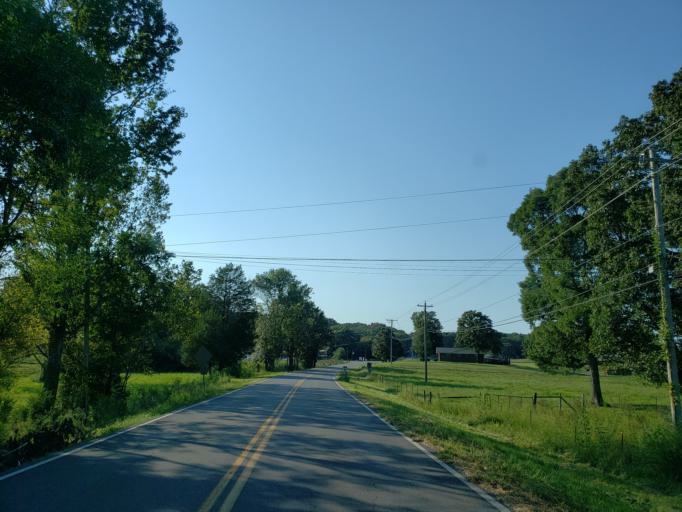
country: US
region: Tennessee
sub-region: Bradley County
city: Wildwood Lake
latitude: 35.0883
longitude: -84.7942
